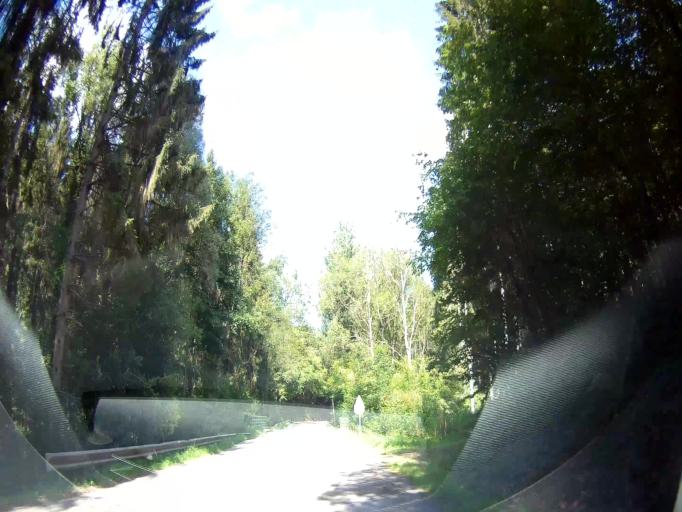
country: BE
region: Wallonia
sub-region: Province de Namur
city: Houyet
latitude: 50.2140
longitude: 4.9708
